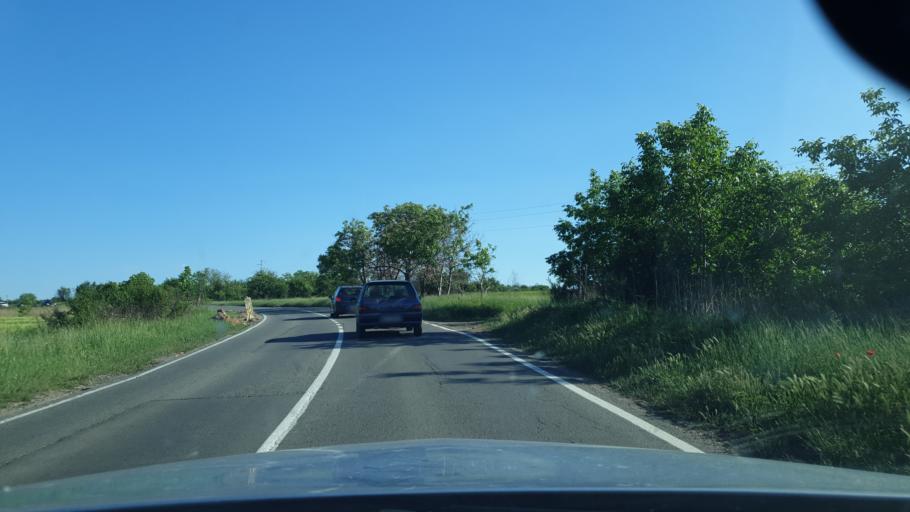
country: RS
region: Central Serbia
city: Sremcica
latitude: 44.7090
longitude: 20.3674
